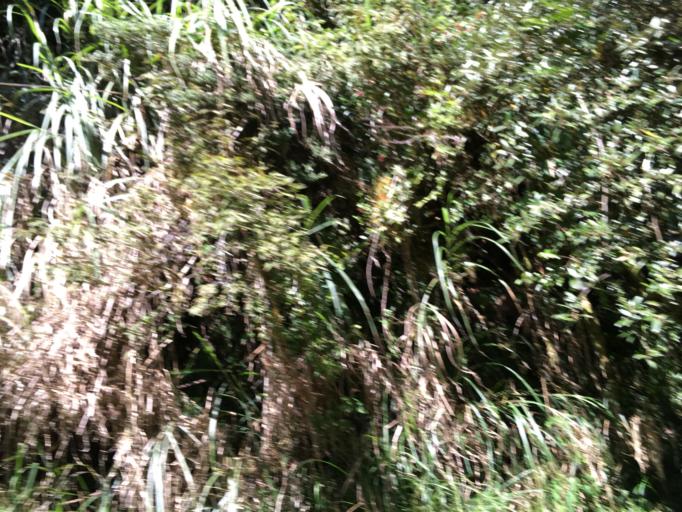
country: TW
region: Taiwan
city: Daxi
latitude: 24.5569
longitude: 121.3976
